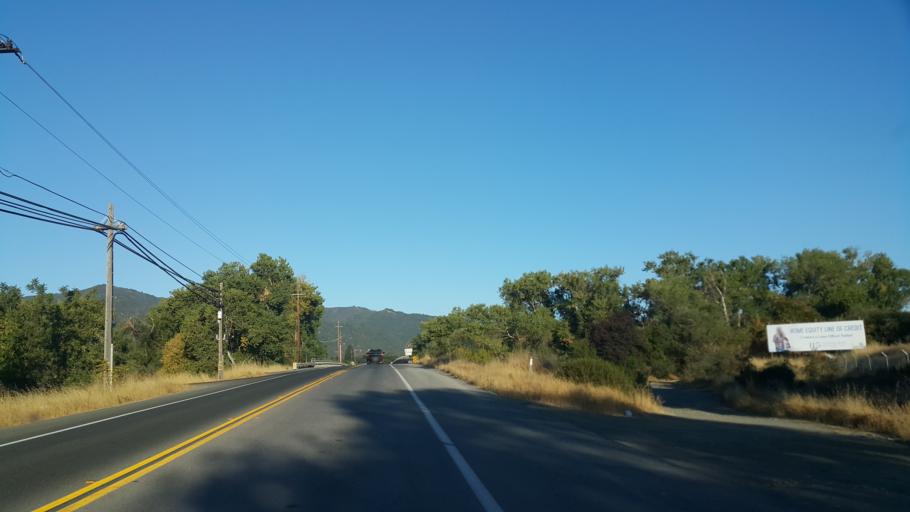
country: US
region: California
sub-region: Mendocino County
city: Talmage
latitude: 39.1339
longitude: -123.1847
